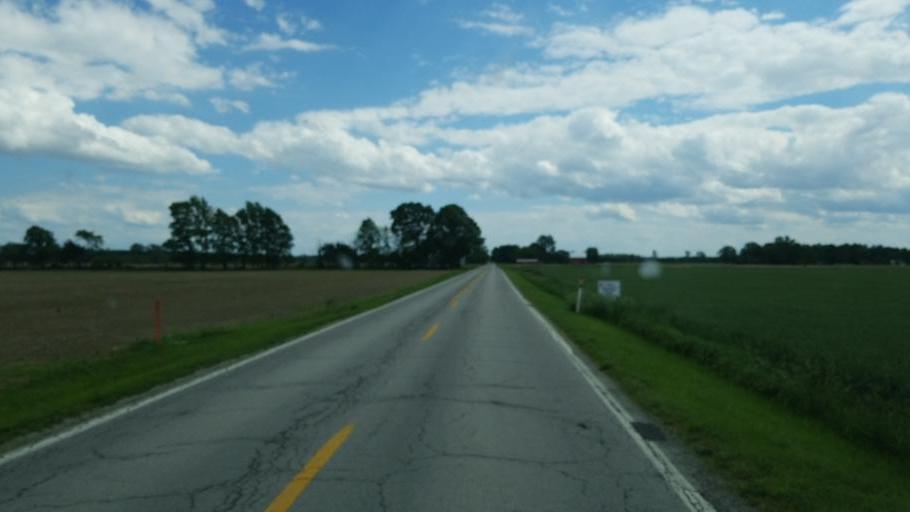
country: US
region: Ohio
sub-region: Huron County
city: Plymouth
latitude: 41.0748
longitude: -82.6106
